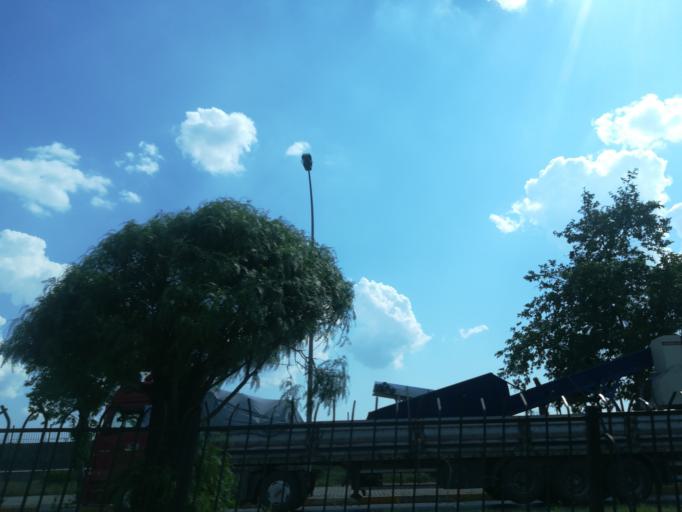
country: TR
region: Adana
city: Yuregir
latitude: 36.9885
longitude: 35.3463
